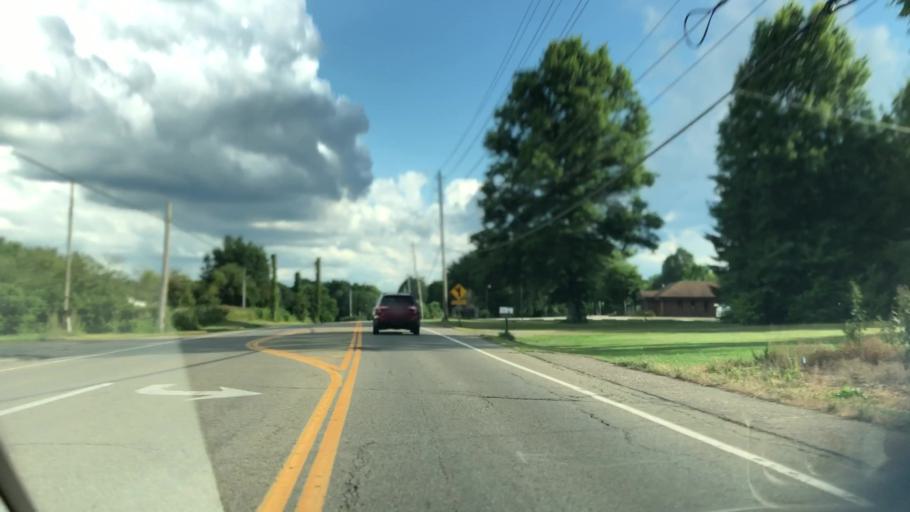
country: US
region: Ohio
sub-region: Summit County
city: Green
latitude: 40.9524
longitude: -81.4946
